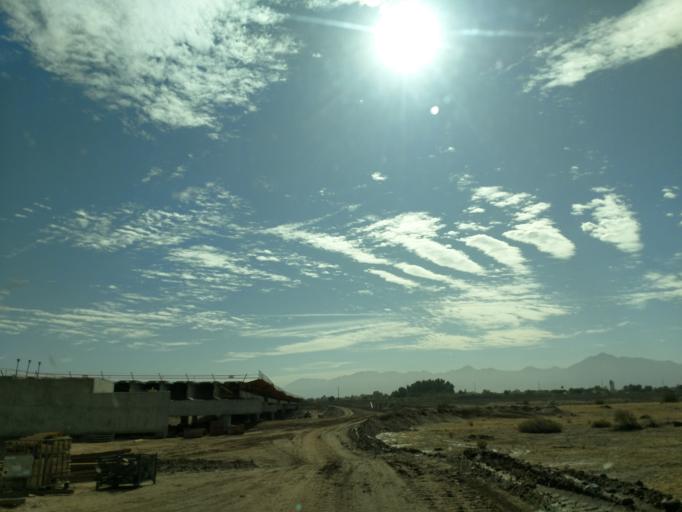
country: US
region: Arizona
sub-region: Maricopa County
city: Laveen
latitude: 33.3979
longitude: -112.1926
